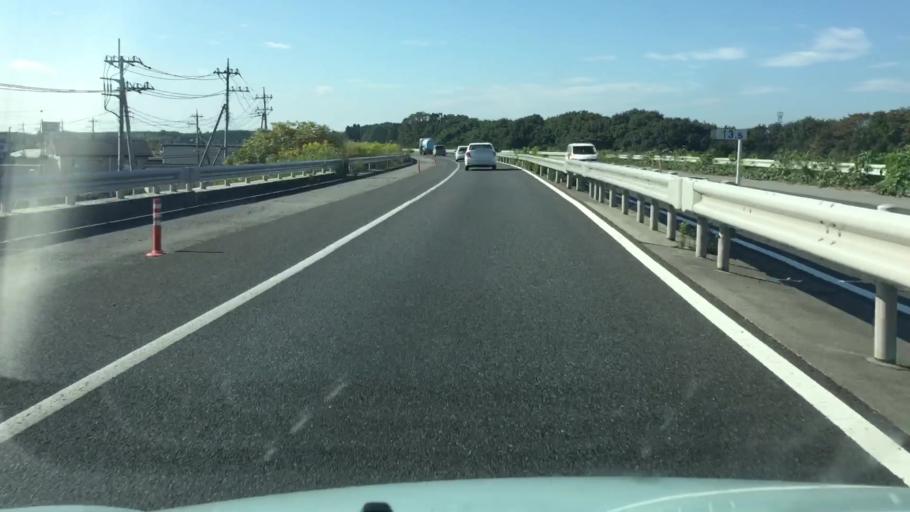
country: JP
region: Tochigi
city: Mooka
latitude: 36.5282
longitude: 139.9849
